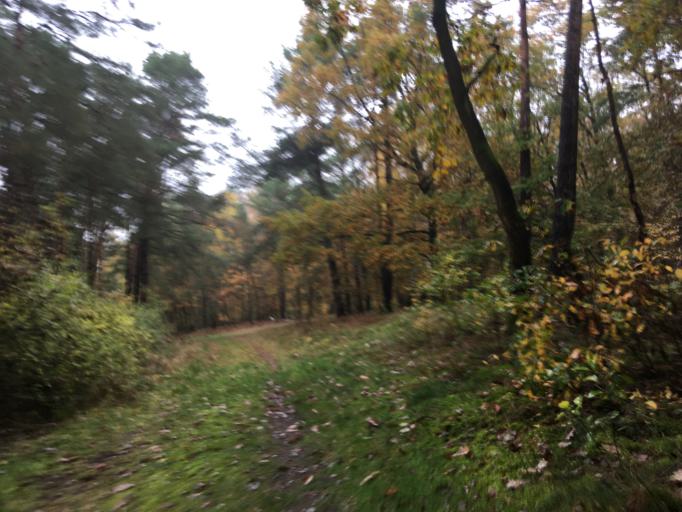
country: DE
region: Brandenburg
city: Briesen
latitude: 52.2635
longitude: 14.2943
